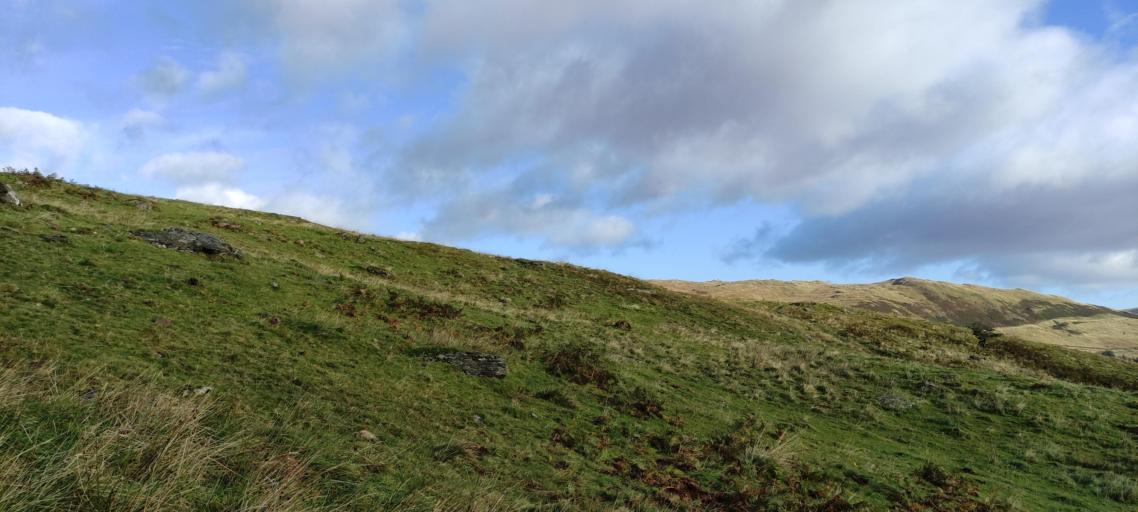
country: GB
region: England
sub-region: Cumbria
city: Kendal
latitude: 54.4118
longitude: -2.7152
